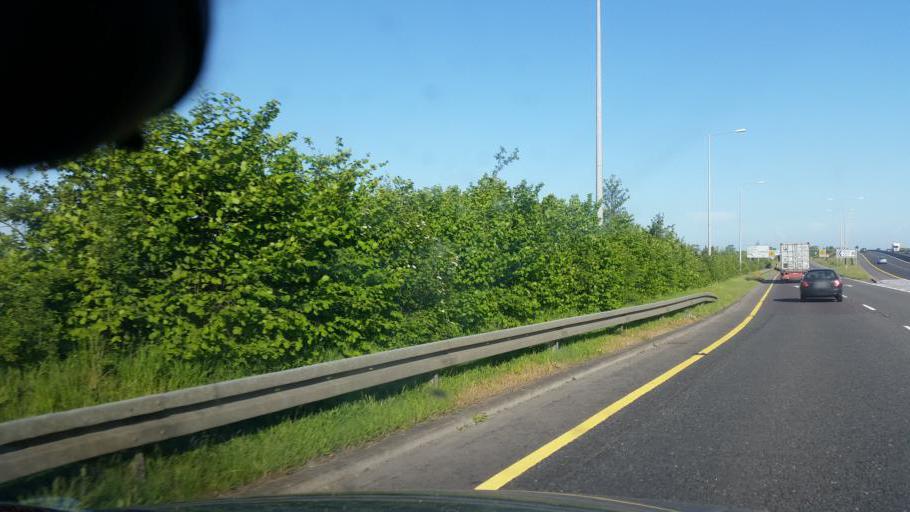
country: IE
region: Leinster
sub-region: Fingal County
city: Blanchardstown
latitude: 53.4296
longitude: -6.3385
